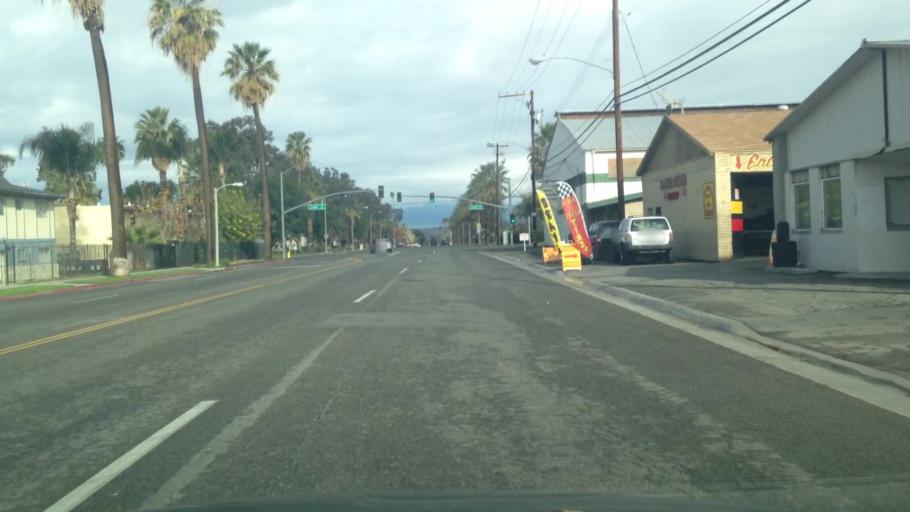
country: US
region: California
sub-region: Riverside County
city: Highgrove
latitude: 33.9784
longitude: -117.3485
